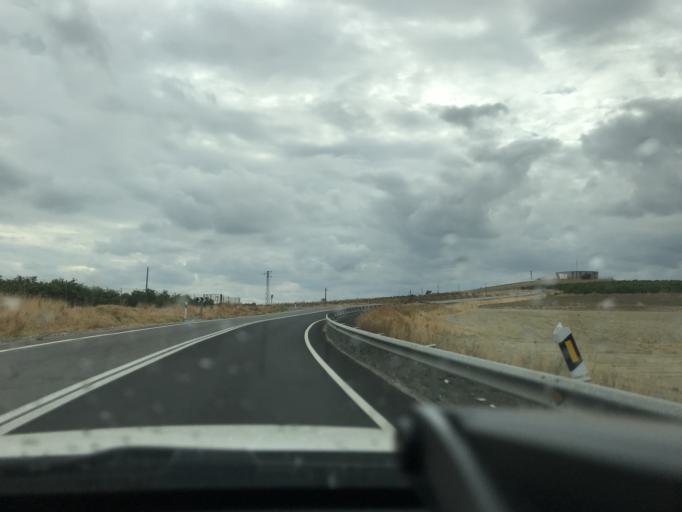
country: ES
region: Andalusia
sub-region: Provincia de Sevilla
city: Cantillana
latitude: 37.6162
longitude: -5.7990
